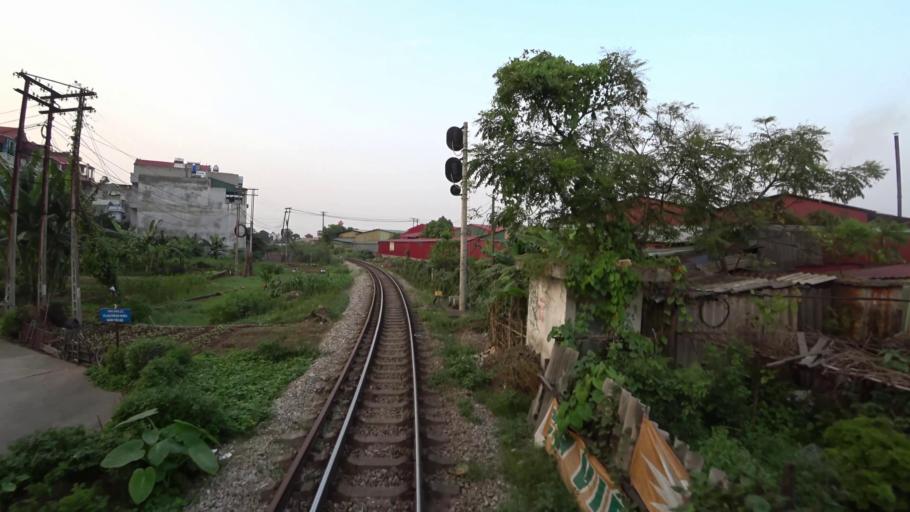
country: VN
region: Ha Noi
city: Dong Anh
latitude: 21.1083
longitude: 105.8982
